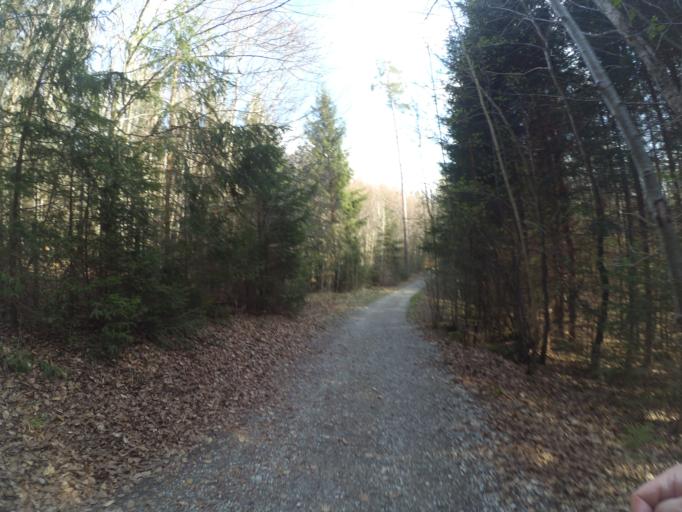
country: DE
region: Bavaria
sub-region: Swabia
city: Bad Worishofen
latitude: 48.0107
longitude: 10.5729
